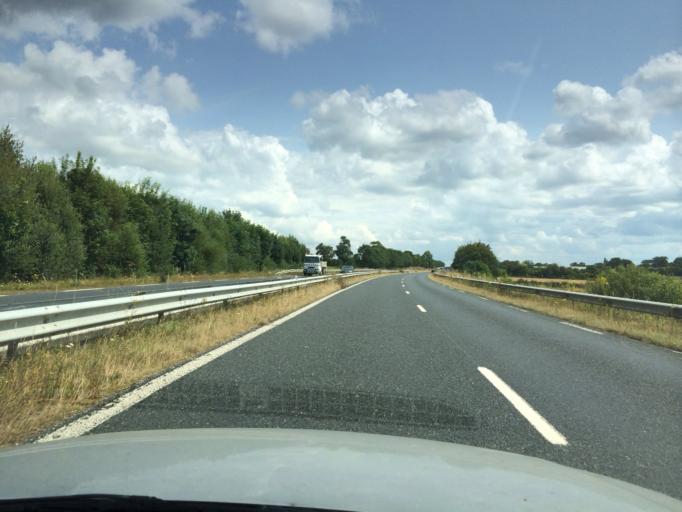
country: FR
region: Lower Normandy
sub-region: Departement du Calvados
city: Grandcamp-Maisy
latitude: 49.3438
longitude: -0.9563
